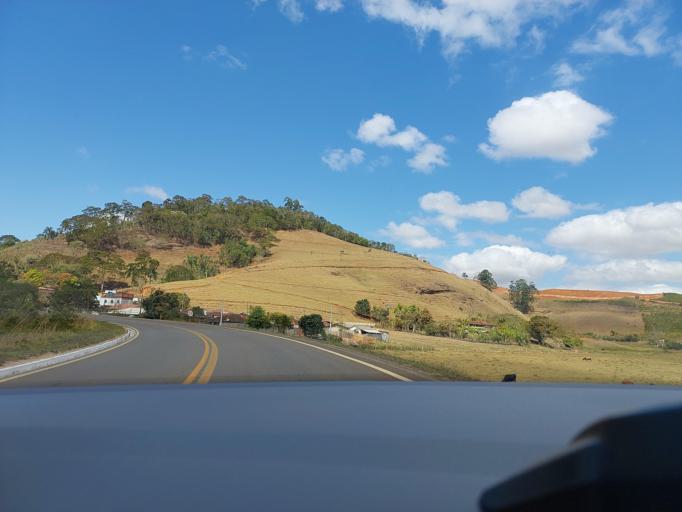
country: BR
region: Minas Gerais
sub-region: Mirai
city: Mirai
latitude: -21.0070
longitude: -42.5533
